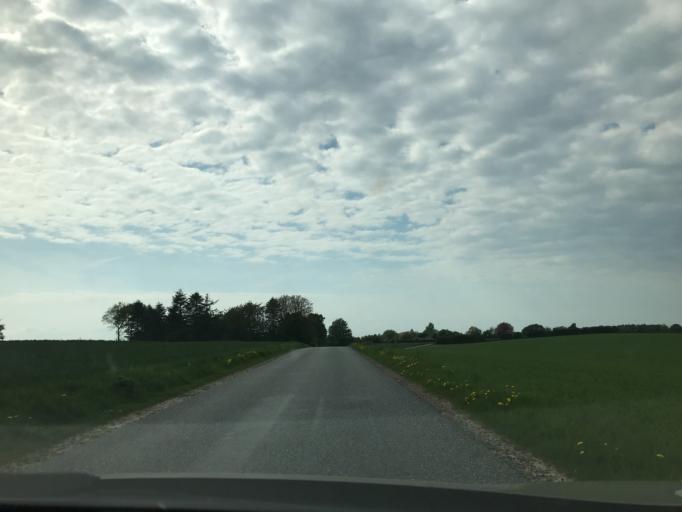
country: DK
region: South Denmark
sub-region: Middelfart Kommune
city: Ejby
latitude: 55.3556
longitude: 9.8883
